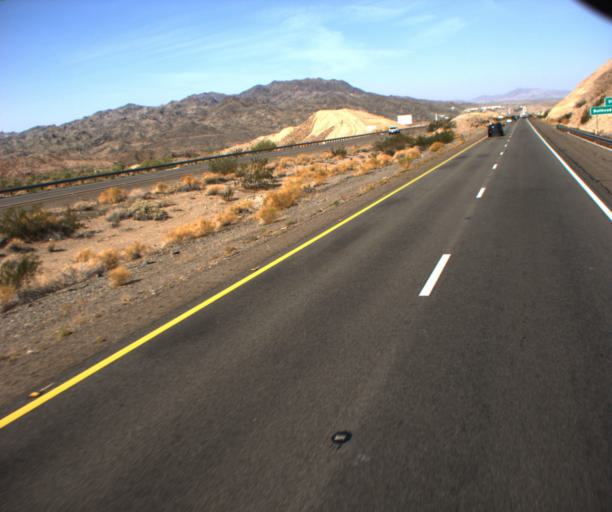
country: US
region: Arizona
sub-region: Mohave County
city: Desert Hills
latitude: 34.7194
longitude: -114.4595
